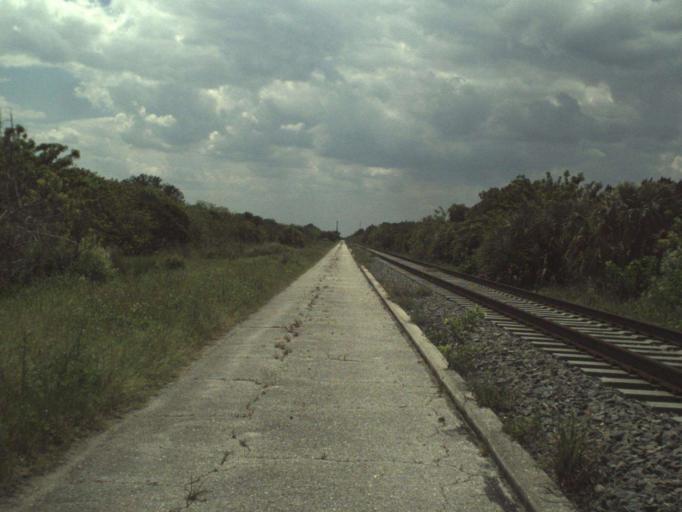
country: US
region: Florida
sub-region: Brevard County
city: Merritt Island
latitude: 28.6434
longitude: -80.6570
